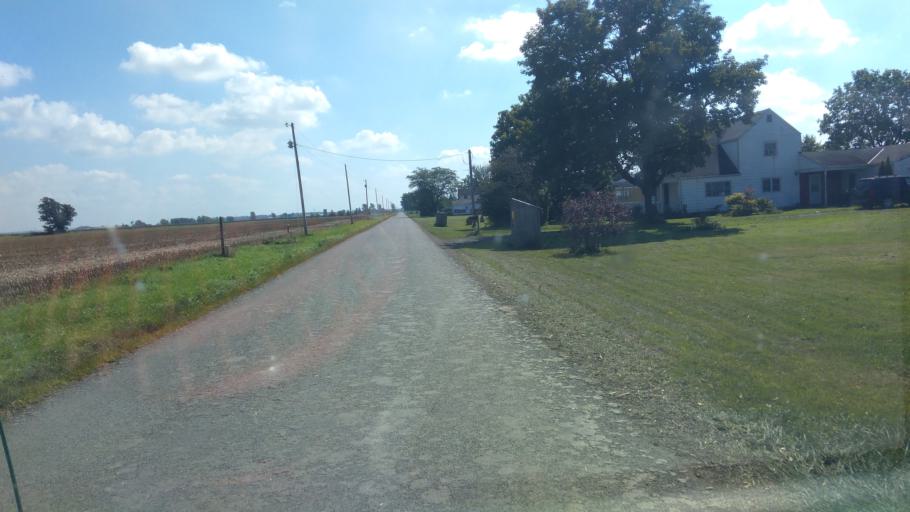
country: US
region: Ohio
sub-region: Hardin County
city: Ada
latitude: 40.6965
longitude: -83.8421
